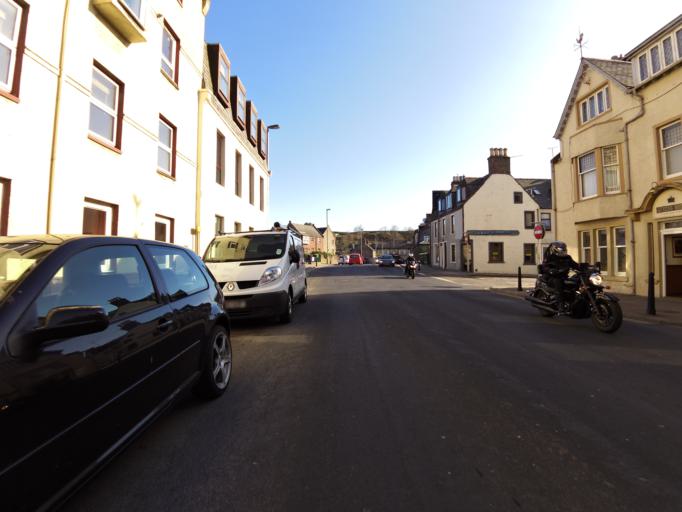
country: GB
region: Scotland
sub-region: Aberdeenshire
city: Stonehaven
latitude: 56.9632
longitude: -2.2081
